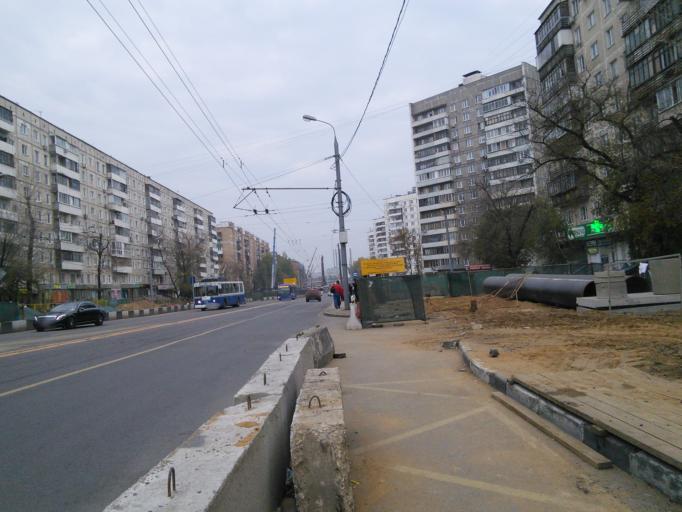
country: RU
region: Moskovskaya
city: Khoroshevo-Mnevniki
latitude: 55.7928
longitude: 37.4920
